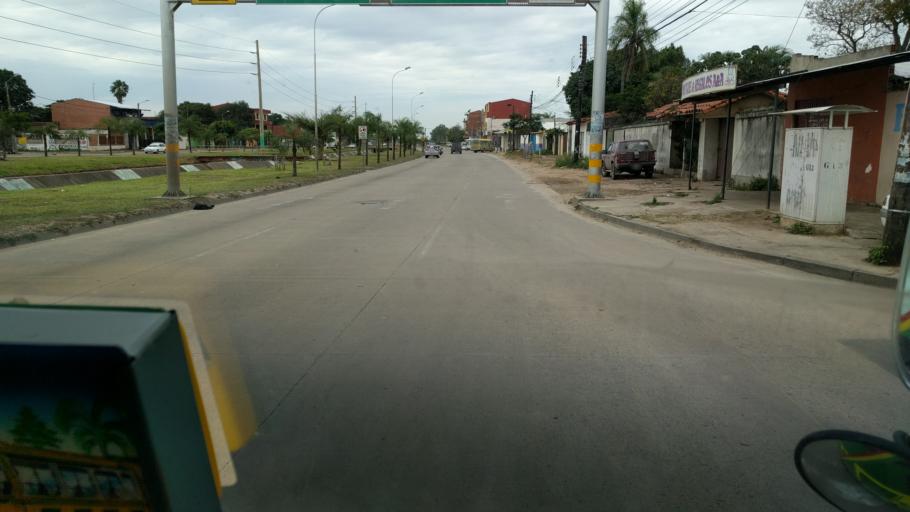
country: BO
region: Santa Cruz
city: Santa Cruz de la Sierra
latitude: -17.8199
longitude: -63.1716
